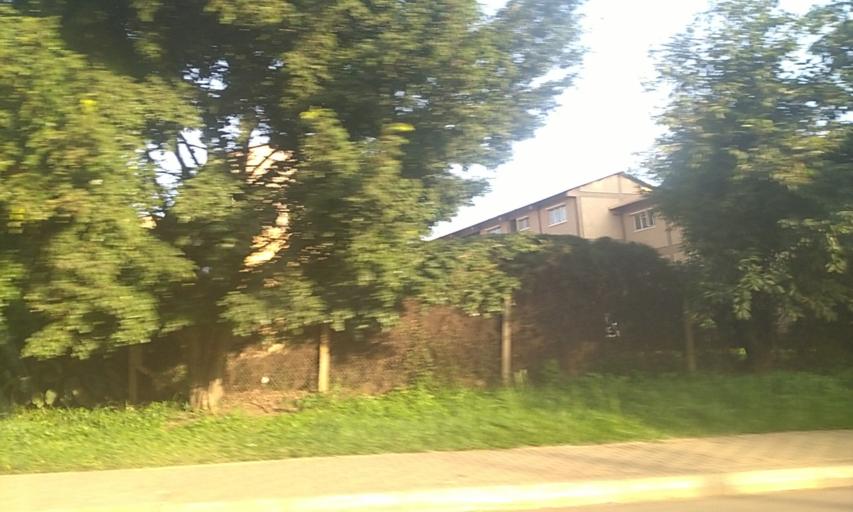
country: UG
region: Central Region
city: Kampala Central Division
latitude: 0.3447
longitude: 32.5964
